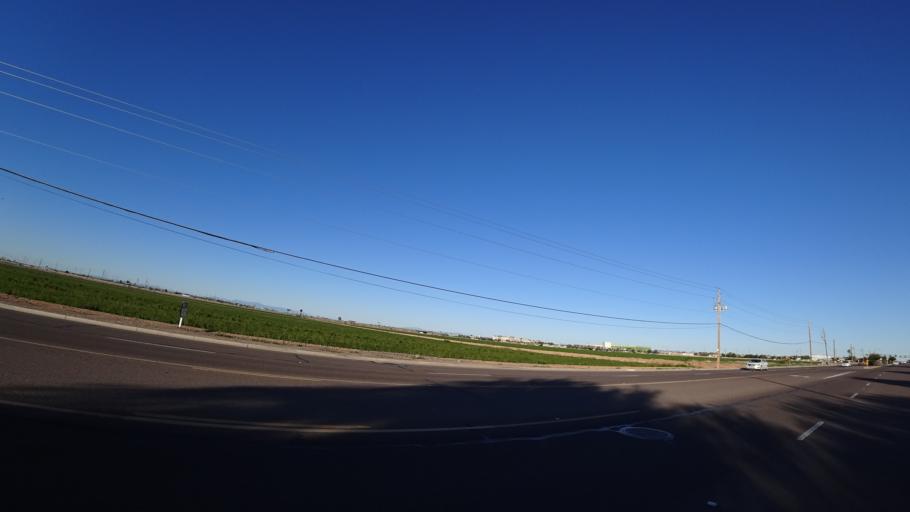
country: US
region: Arizona
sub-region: Maricopa County
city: Avondale
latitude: 33.4496
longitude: -112.3121
